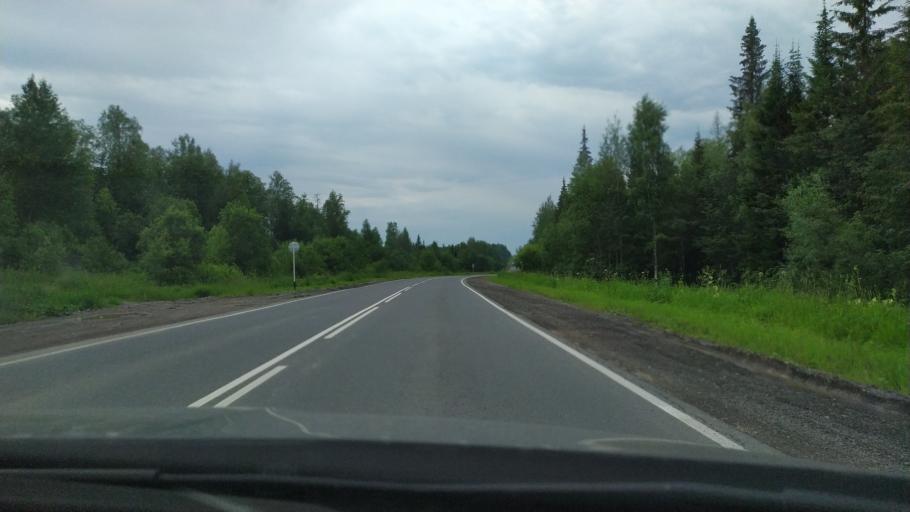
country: RU
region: Perm
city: Gremyachinsk
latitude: 58.4258
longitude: 57.8821
